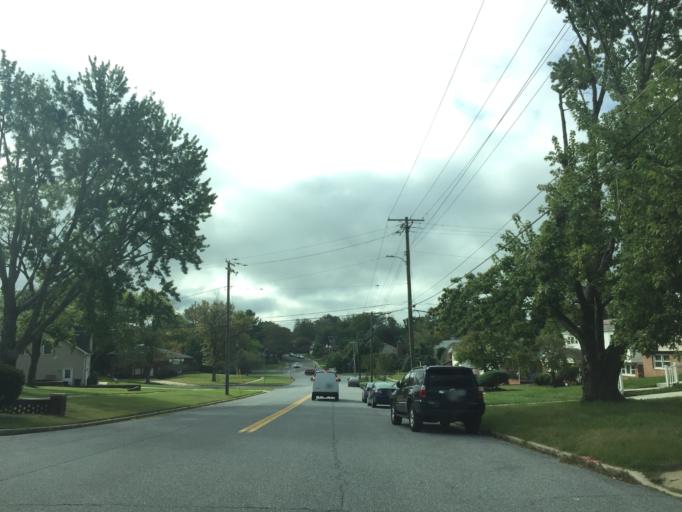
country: US
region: Maryland
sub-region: Baltimore County
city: Pikesville
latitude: 39.3736
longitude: -76.6782
